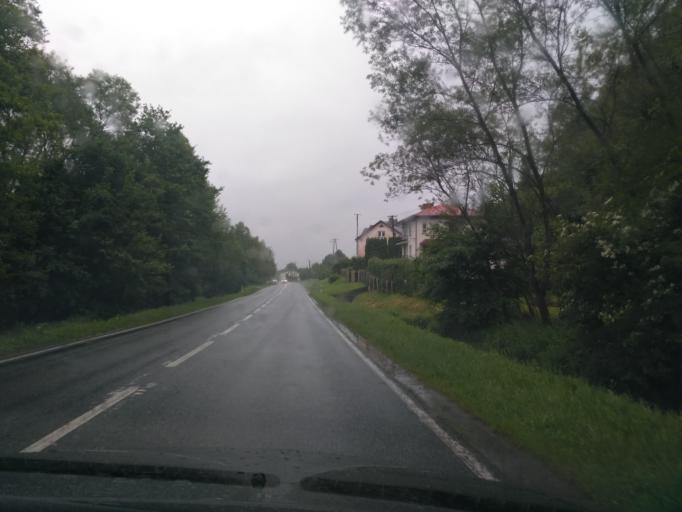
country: PL
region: Subcarpathian Voivodeship
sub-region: Powiat krosnienski
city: Leki
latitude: 49.8034
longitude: 21.6406
